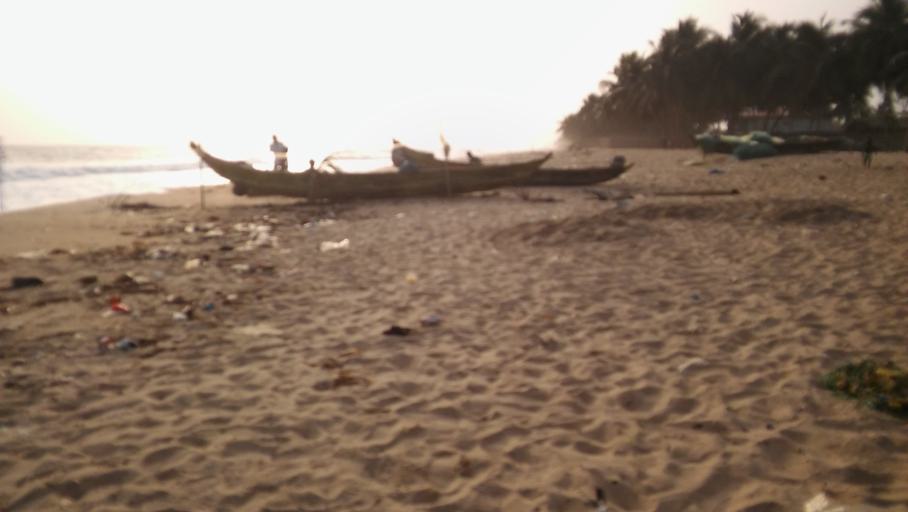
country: CI
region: Sud-Comoe
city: Grand-Bassam
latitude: 5.1921
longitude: -3.7258
